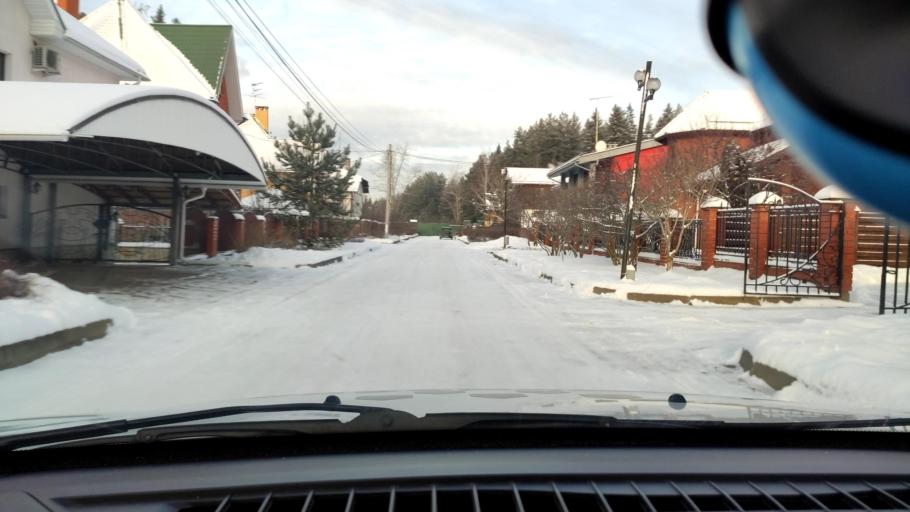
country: RU
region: Perm
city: Kondratovo
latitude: 58.0510
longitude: 56.1015
